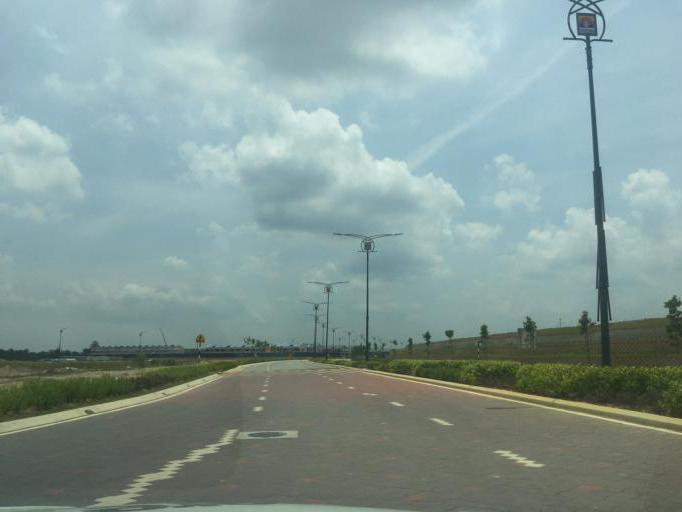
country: MY
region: Putrajaya
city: Putrajaya
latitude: 2.8457
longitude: 101.7064
